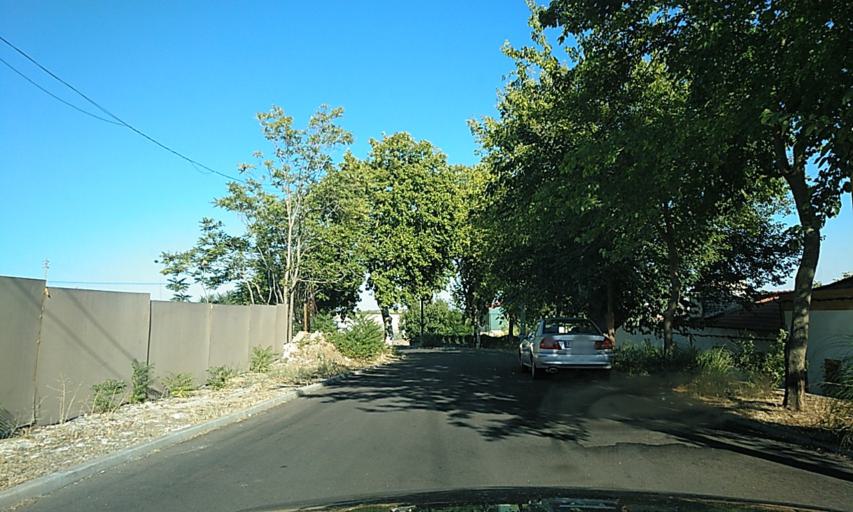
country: PT
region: Portalegre
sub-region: Campo Maior
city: Campo Maior
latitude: 39.0108
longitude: -7.0650
